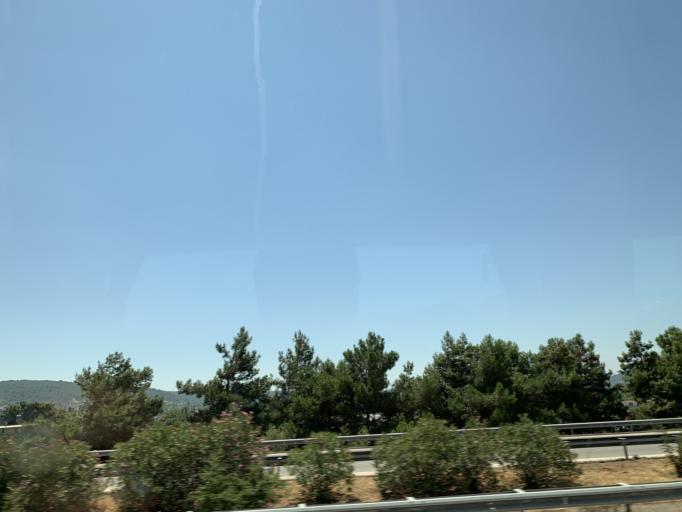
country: TR
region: Izmir
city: Urla
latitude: 38.3007
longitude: 26.7445
